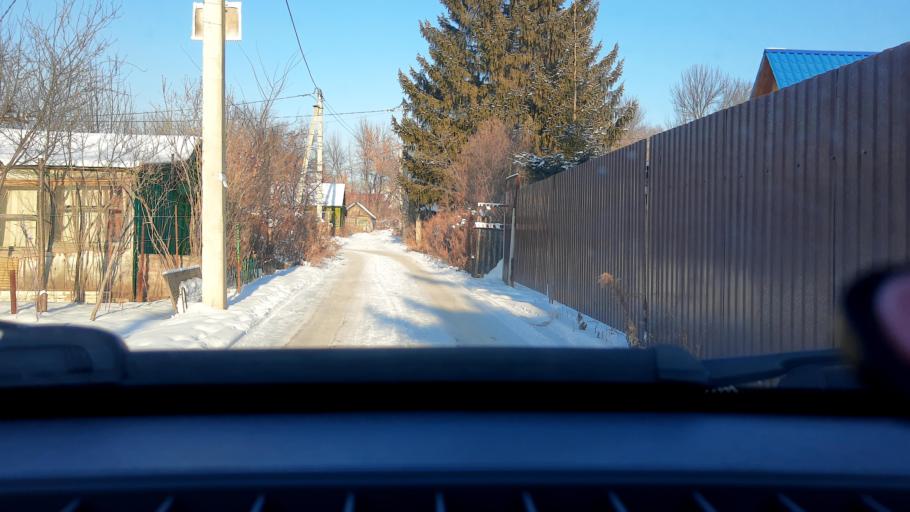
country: RU
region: Bashkortostan
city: Ufa
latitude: 54.7970
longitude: 56.1567
